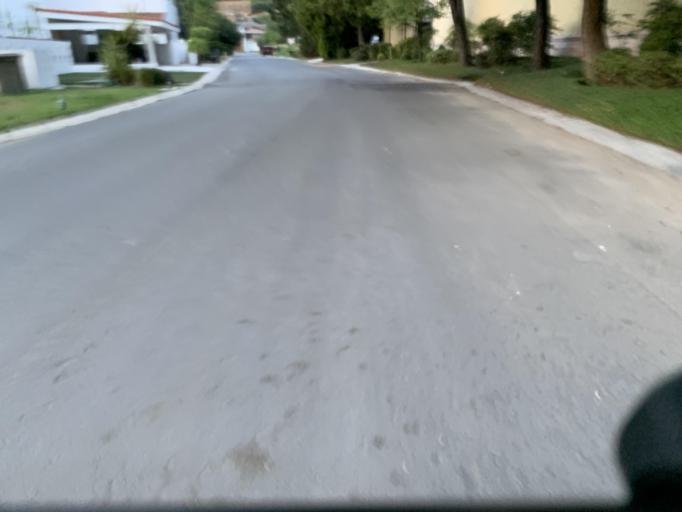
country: MX
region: Nuevo Leon
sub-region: Juarez
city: Bosques de San Pedro
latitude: 25.5209
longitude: -100.1936
